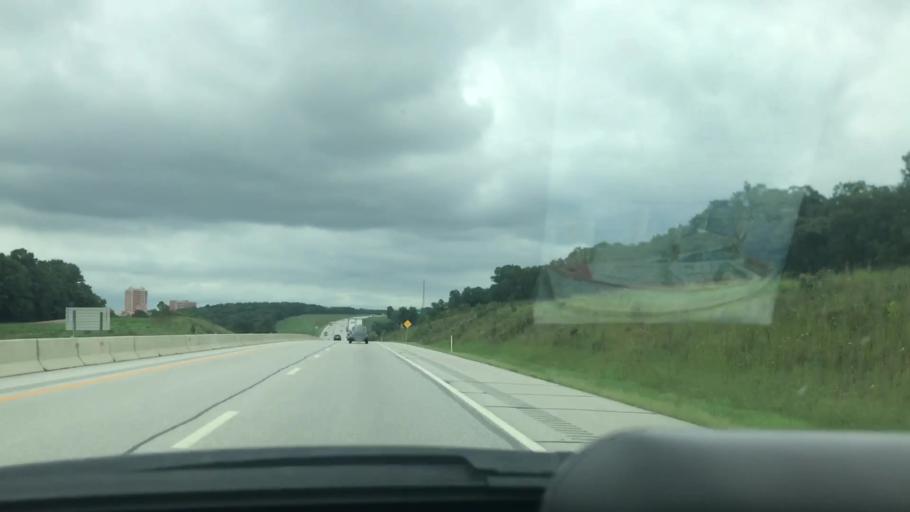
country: US
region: Kansas
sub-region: Cherokee County
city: Galena
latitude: 36.9813
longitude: -94.6362
